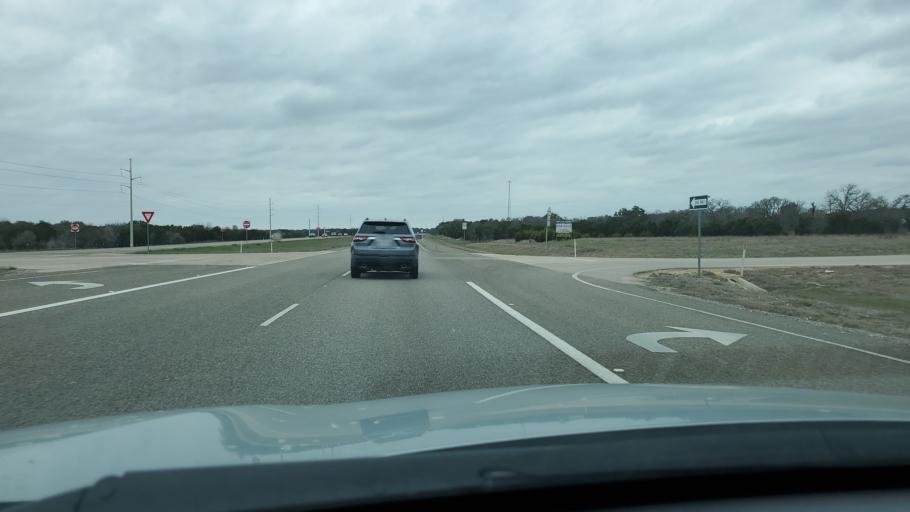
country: US
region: Texas
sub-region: Williamson County
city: Serenada
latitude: 30.7640
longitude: -97.7473
